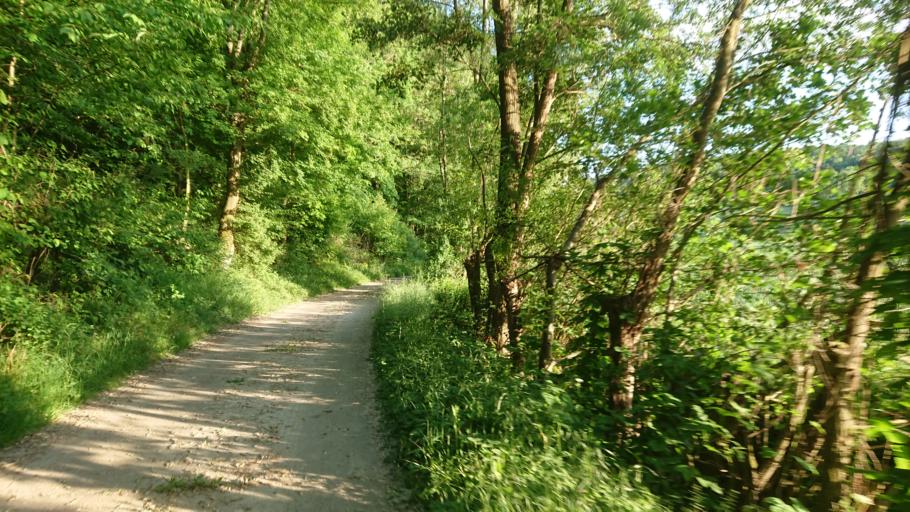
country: DE
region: Lower Saxony
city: Hardegsen
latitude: 51.6015
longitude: 9.8383
